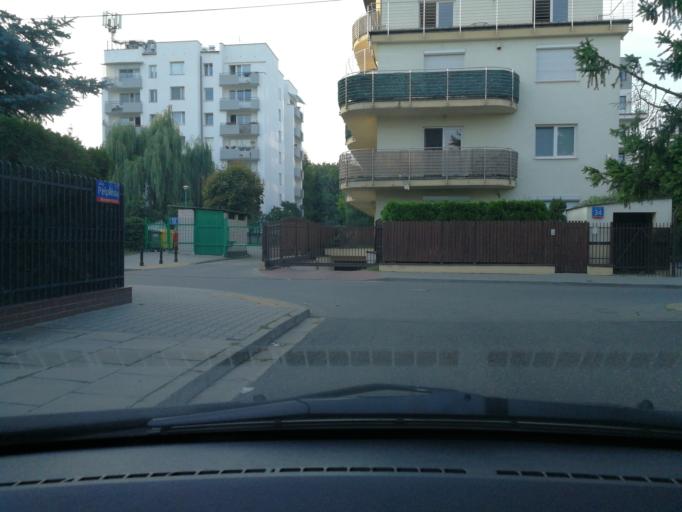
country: PL
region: Masovian Voivodeship
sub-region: Warszawa
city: Zoliborz
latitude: 52.2833
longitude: 20.9692
